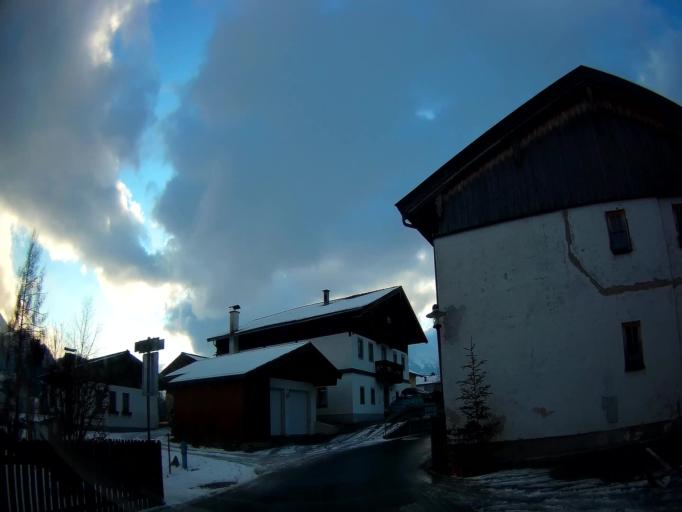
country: AT
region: Salzburg
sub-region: Politischer Bezirk Zell am See
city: Saalfelden am Steinernen Meer
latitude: 47.4499
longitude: 12.8192
